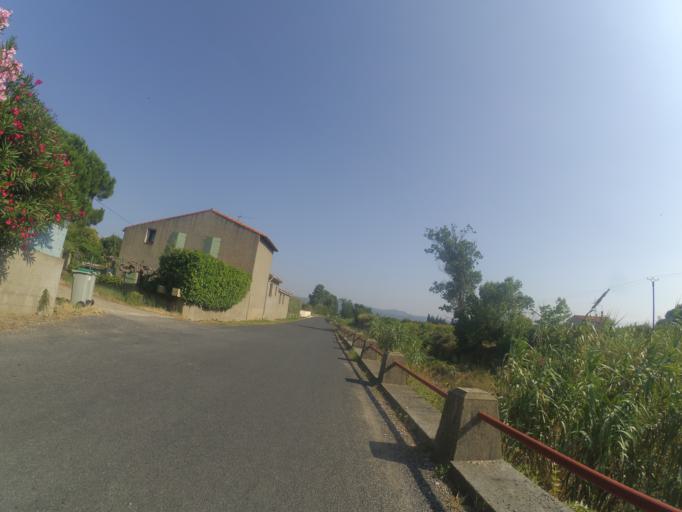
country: FR
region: Languedoc-Roussillon
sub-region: Departement des Pyrenees-Orientales
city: Ille-sur-Tet
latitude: 42.6527
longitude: 2.6234
